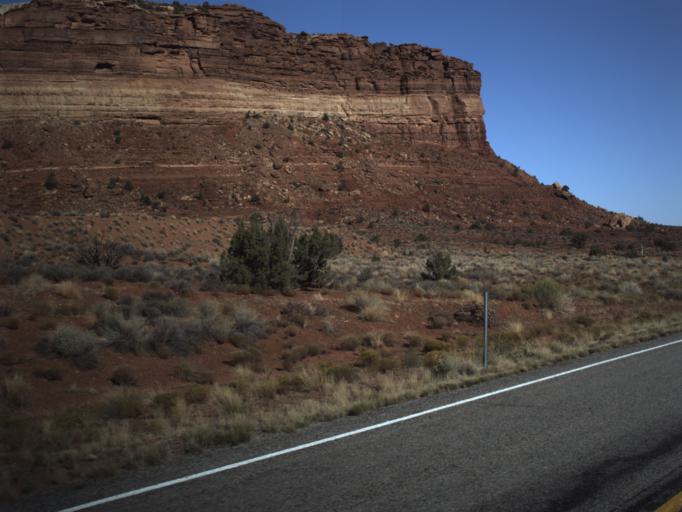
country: US
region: Utah
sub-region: San Juan County
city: Blanding
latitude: 37.7487
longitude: -110.2803
